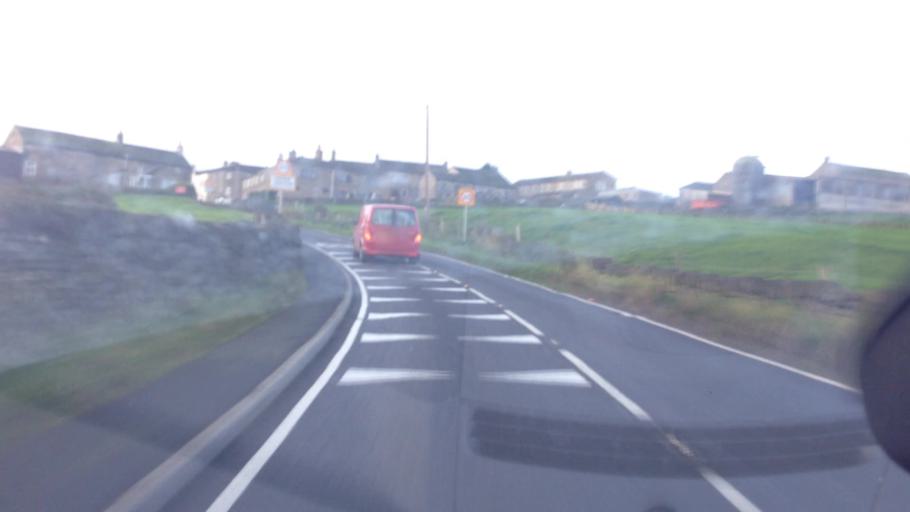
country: GB
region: England
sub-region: Kirklees
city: Mirfield
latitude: 53.6696
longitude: -1.7323
